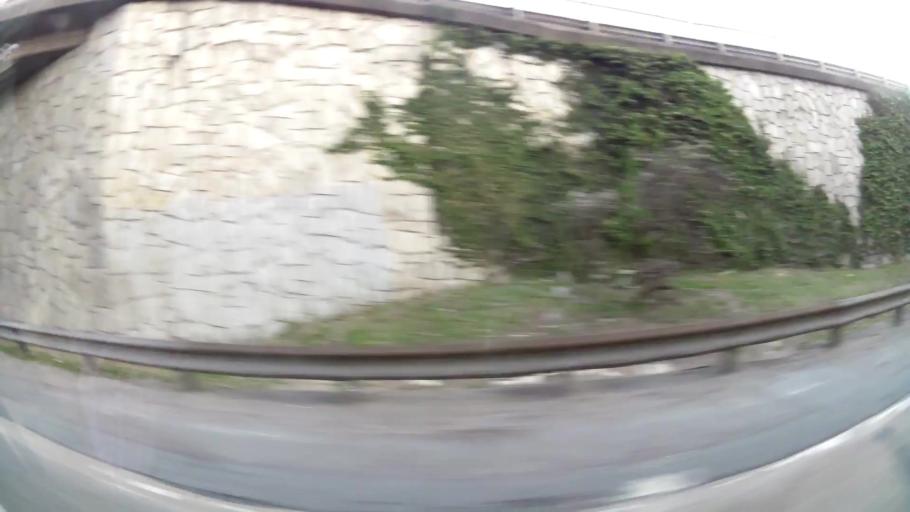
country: AR
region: Buenos Aires
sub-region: Partido de Vicente Lopez
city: Olivos
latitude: -34.5438
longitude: -58.4855
